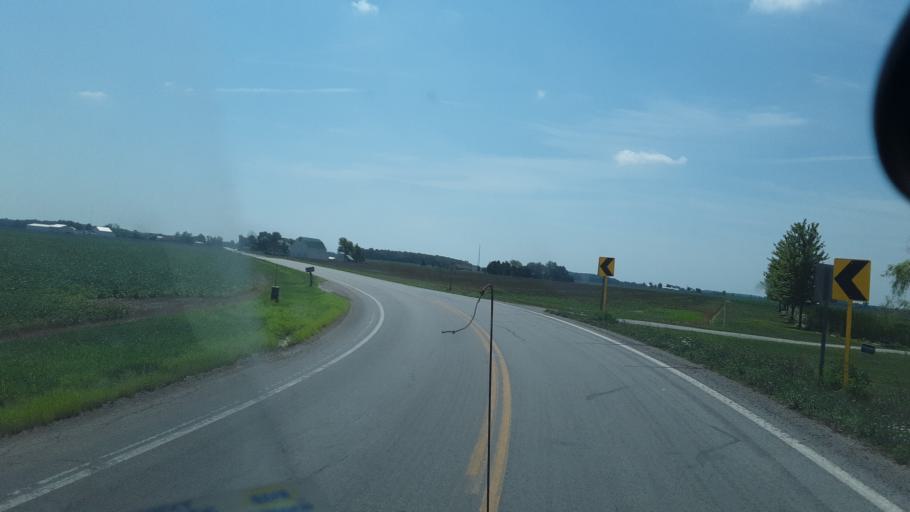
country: US
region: Ohio
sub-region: Hancock County
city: Arlington
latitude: 40.9417
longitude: -83.5750
